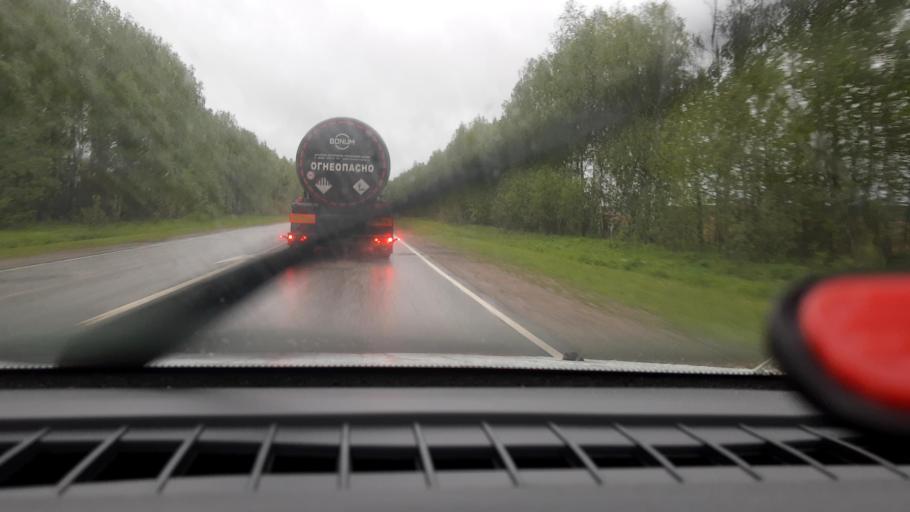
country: RU
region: Nizjnij Novgorod
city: Vladimirskoye
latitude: 56.9166
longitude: 45.0539
